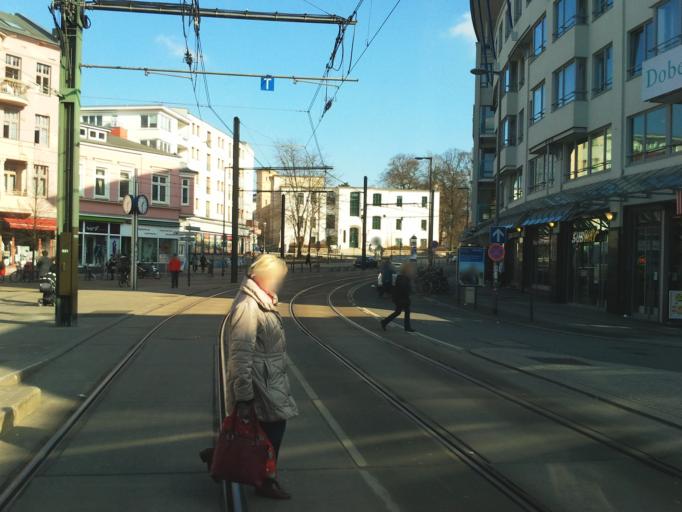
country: DE
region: Mecklenburg-Vorpommern
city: Rostock
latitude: 54.0881
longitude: 12.1233
